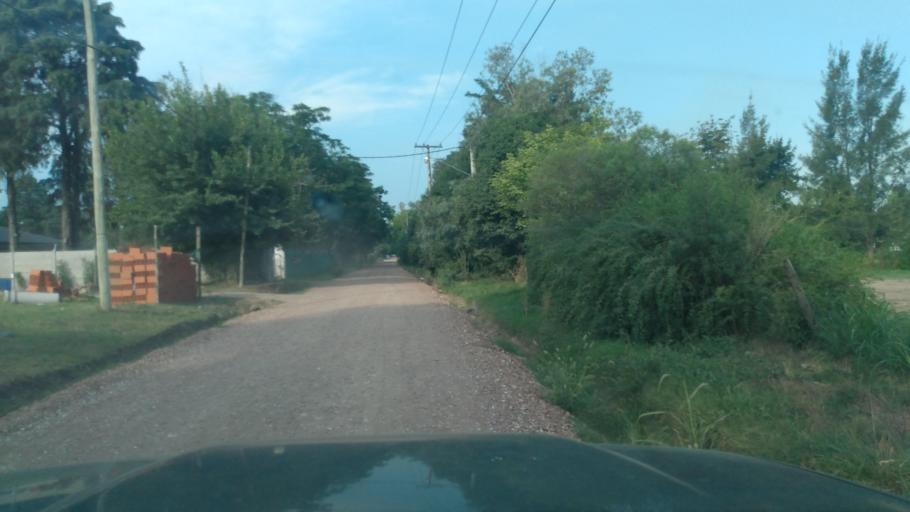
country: AR
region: Buenos Aires
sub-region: Partido de Lujan
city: Lujan
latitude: -34.5493
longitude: -59.1316
